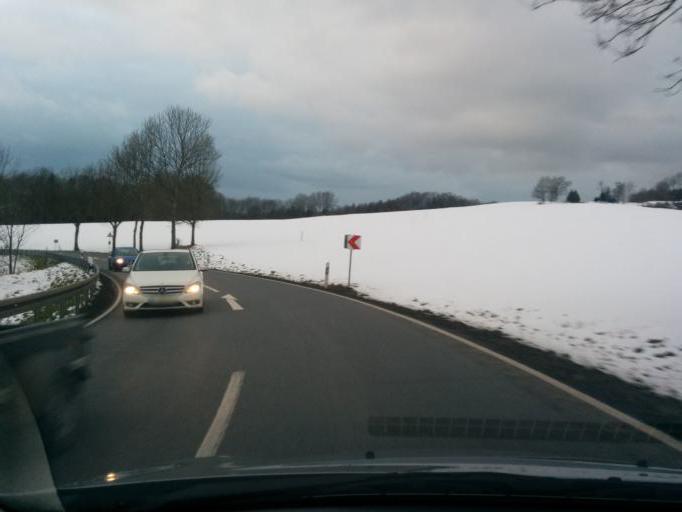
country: DE
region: Saxony
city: Augustusburg
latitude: 50.8291
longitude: 13.0966
